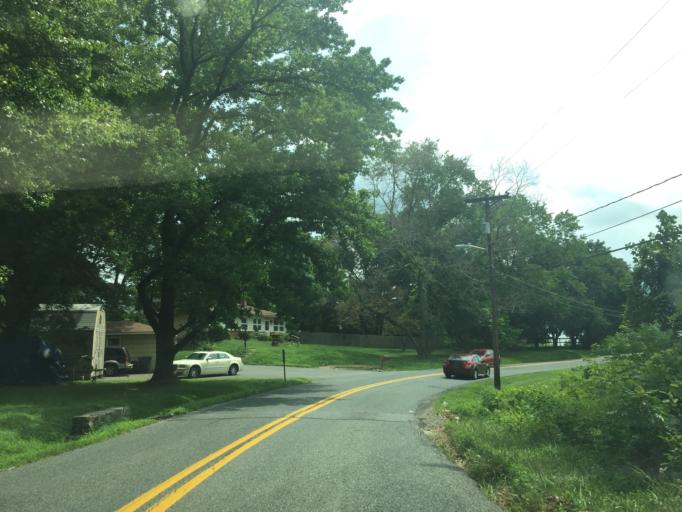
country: US
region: Maryland
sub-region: Baltimore County
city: White Marsh
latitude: 39.3940
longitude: -76.4277
